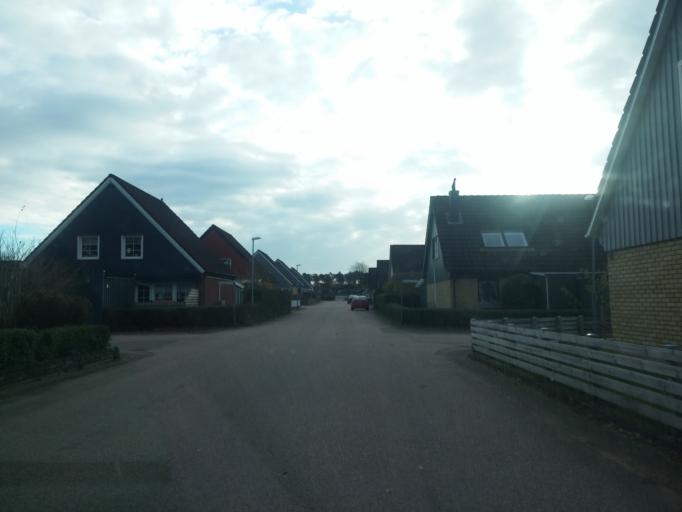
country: SE
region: Skane
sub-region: Angelholms Kommun
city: AEngelholm
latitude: 56.2330
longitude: 12.8399
